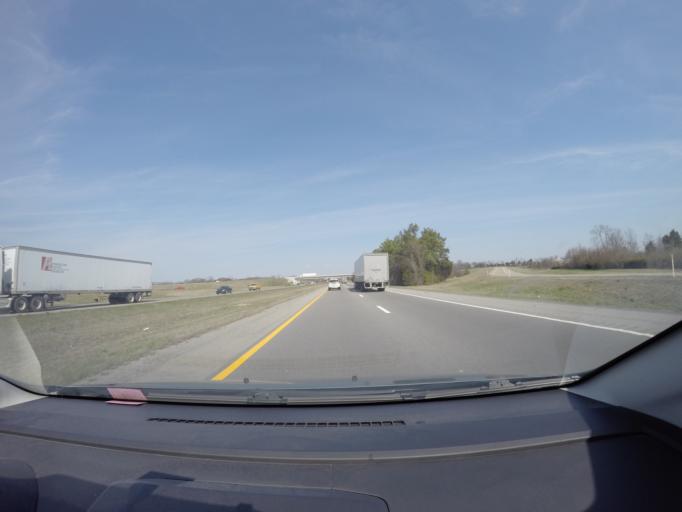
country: US
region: Tennessee
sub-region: Rutherford County
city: Murfreesboro
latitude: 35.7825
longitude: -86.3706
